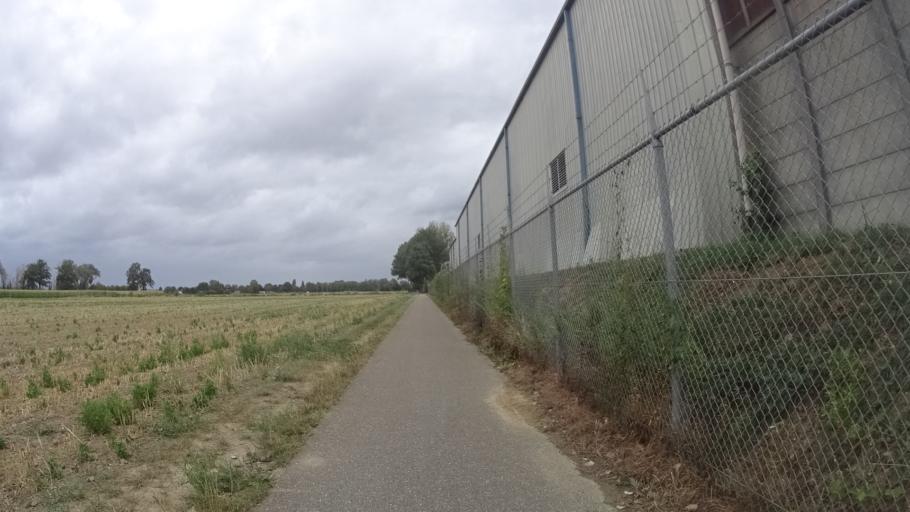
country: NL
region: Limburg
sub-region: Gemeente Maastricht
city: Maastricht
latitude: 50.8863
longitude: 5.7051
